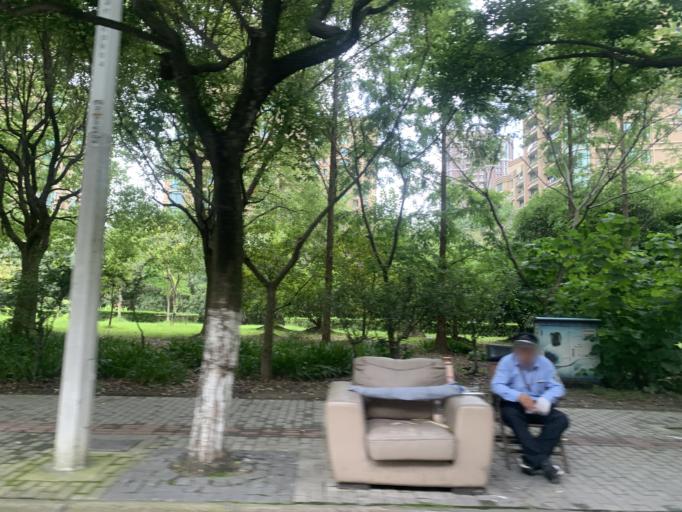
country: CN
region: Shanghai Shi
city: Huamu
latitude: 31.2061
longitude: 121.5312
